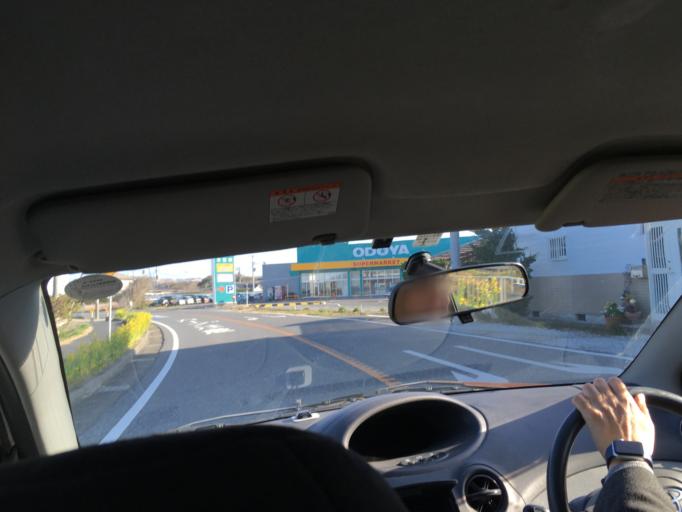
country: JP
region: Chiba
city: Tateyama
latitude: 34.9253
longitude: 139.8319
